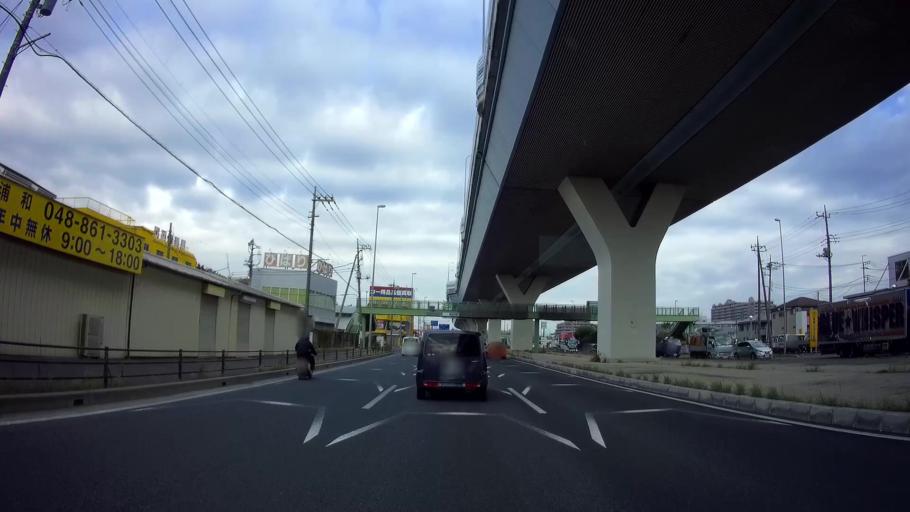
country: JP
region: Saitama
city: Yono
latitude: 35.8569
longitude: 139.6224
